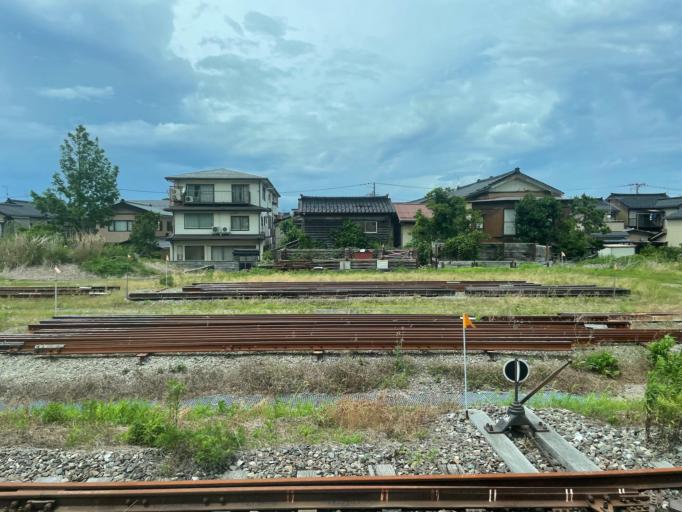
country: JP
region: Niigata
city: Itoigawa
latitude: 37.0568
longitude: 137.9088
